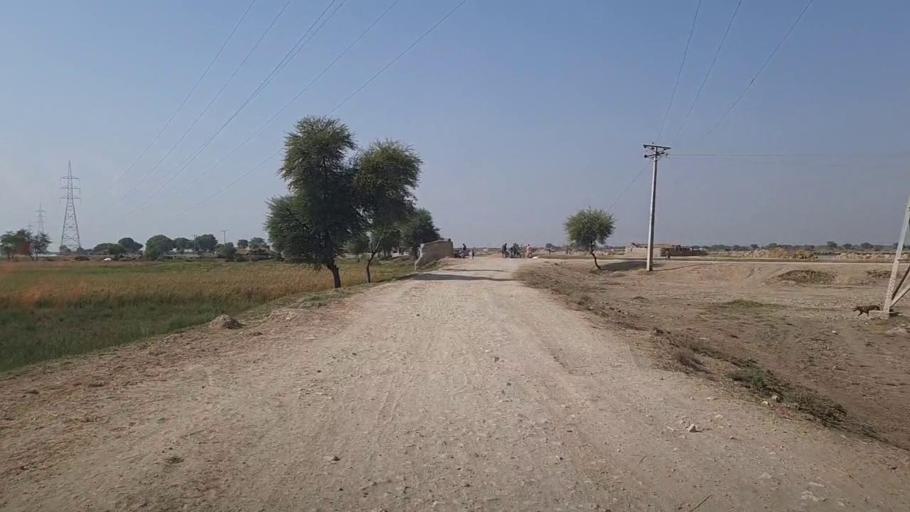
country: PK
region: Sindh
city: Kandhkot
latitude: 28.4116
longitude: 69.2433
